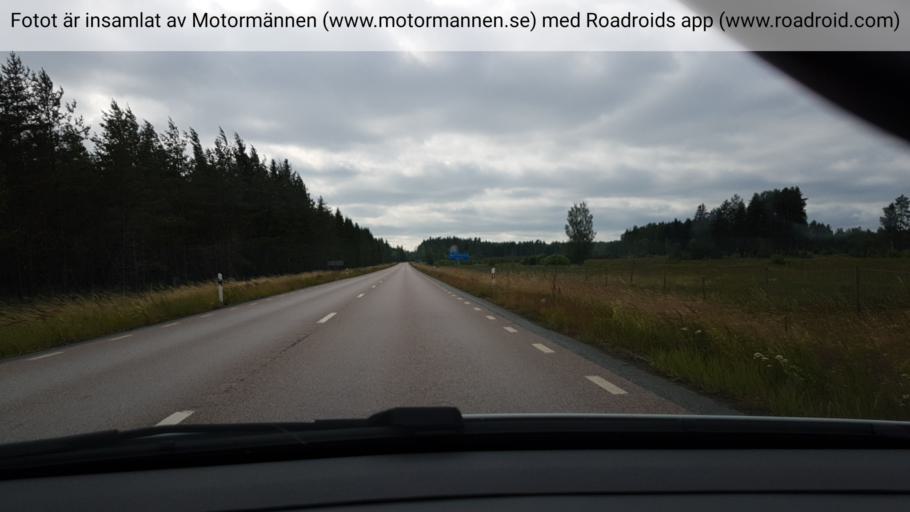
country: SE
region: Uppsala
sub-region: Osthammars Kommun
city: Osterbybruk
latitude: 60.3961
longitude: 17.9093
